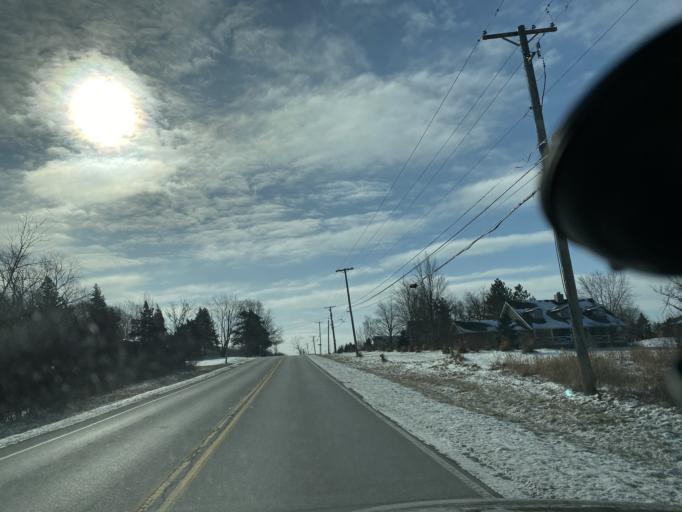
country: US
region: Illinois
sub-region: Will County
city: Goodings Grove
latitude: 41.6638
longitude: -87.9320
